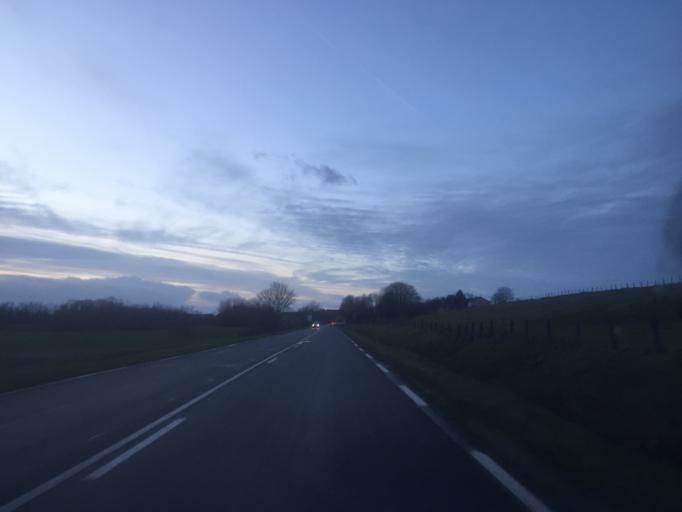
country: FR
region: Franche-Comte
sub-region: Departement du Jura
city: Orchamps
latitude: 47.1438
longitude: 5.6731
